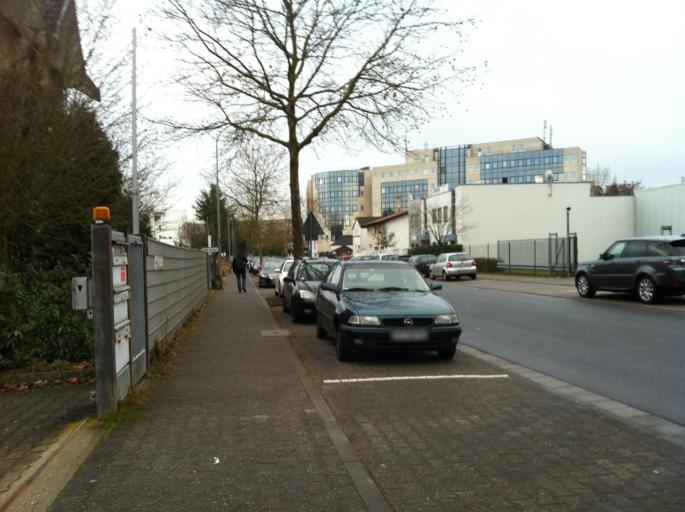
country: DE
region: Hesse
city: Langen
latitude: 50.0053
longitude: 8.6571
